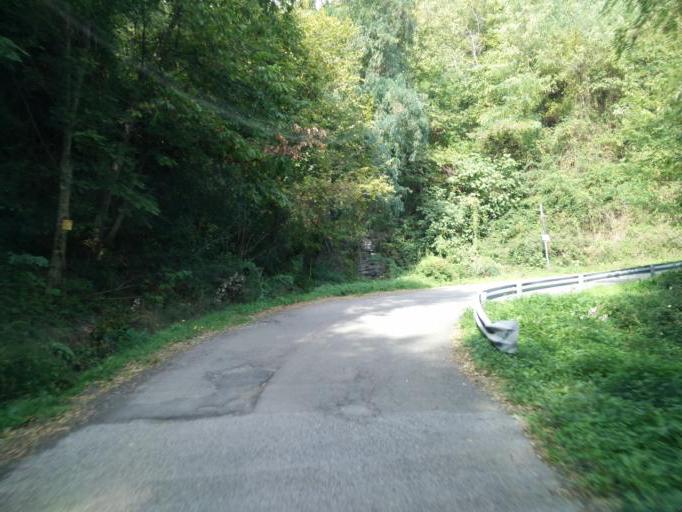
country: IT
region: Liguria
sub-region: Provincia di La Spezia
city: Sesta Godano
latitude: 44.3353
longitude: 9.6969
